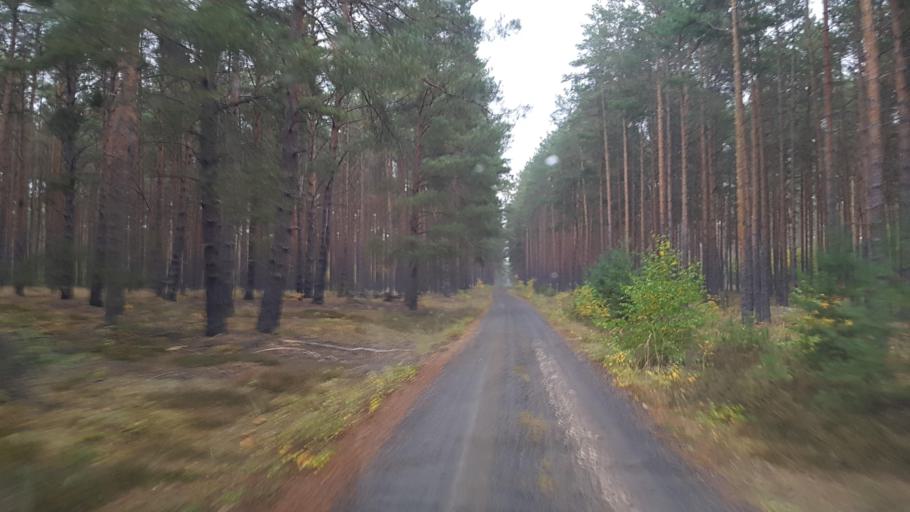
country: DE
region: Brandenburg
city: Schlieben
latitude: 51.7429
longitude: 13.3920
